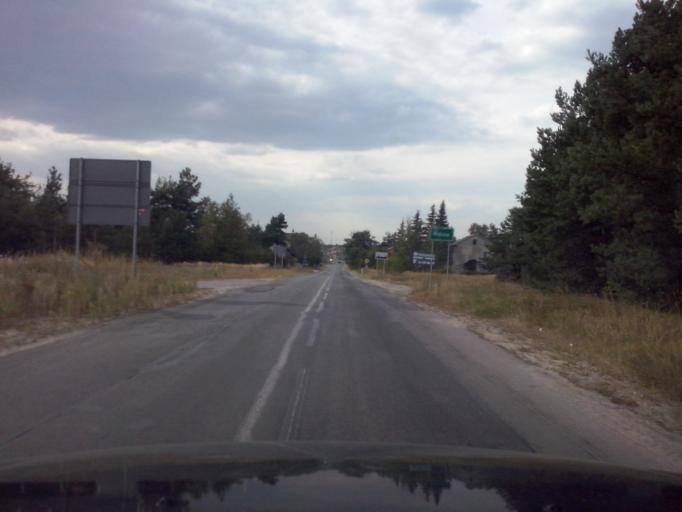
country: PL
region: Swietokrzyskie
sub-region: Powiat kielecki
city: Rakow
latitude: 50.6706
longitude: 21.0516
